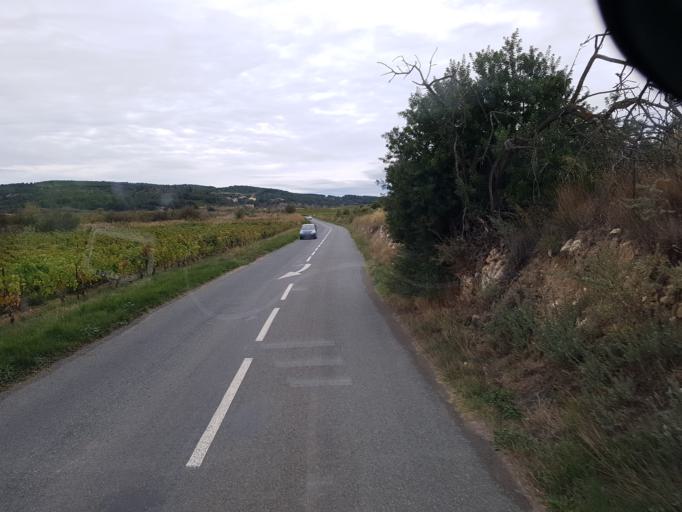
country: FR
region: Languedoc-Roussillon
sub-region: Departement de l'Aude
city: Narbonne
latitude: 43.1423
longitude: 2.9829
